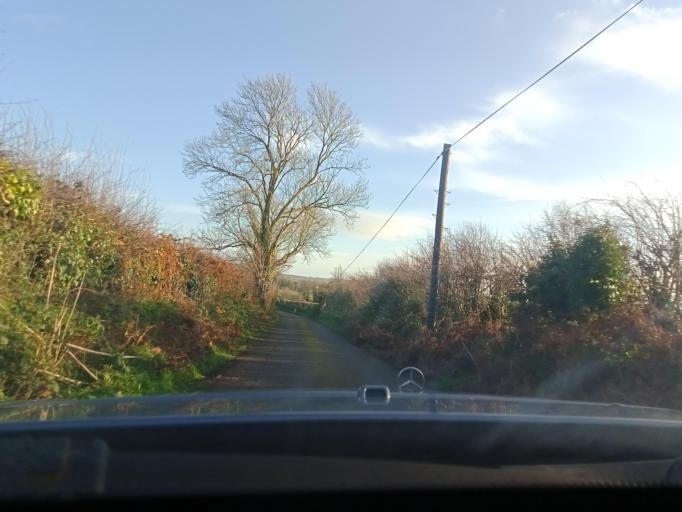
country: IE
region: Munster
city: Carrick-on-Suir
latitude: 52.4367
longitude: -7.4134
